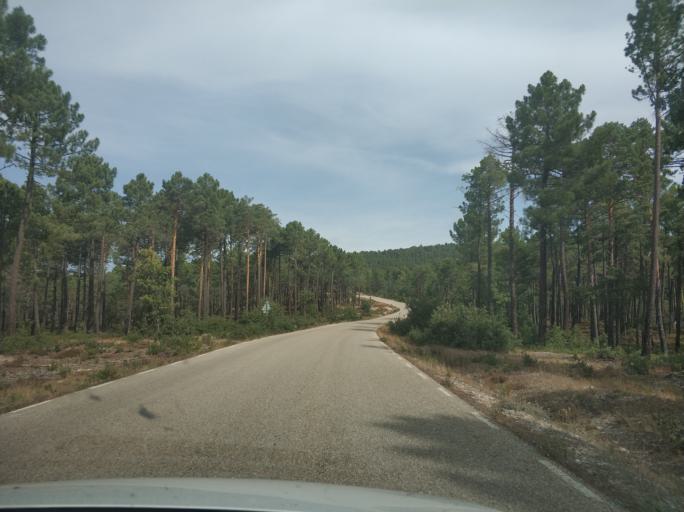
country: ES
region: Castille and Leon
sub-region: Provincia de Soria
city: Duruelo de la Sierra
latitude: 41.8835
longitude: -2.9374
